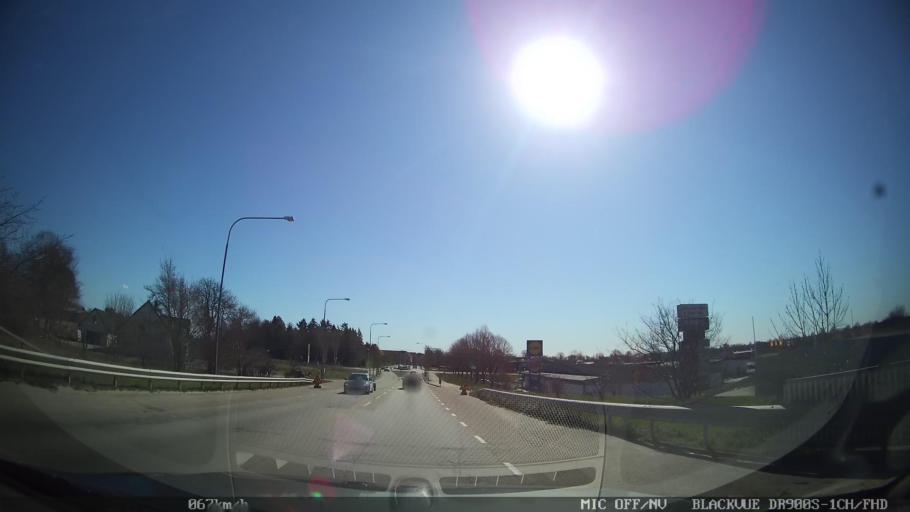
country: SE
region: Skane
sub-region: Ystads Kommun
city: Ystad
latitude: 55.4343
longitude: 13.7992
